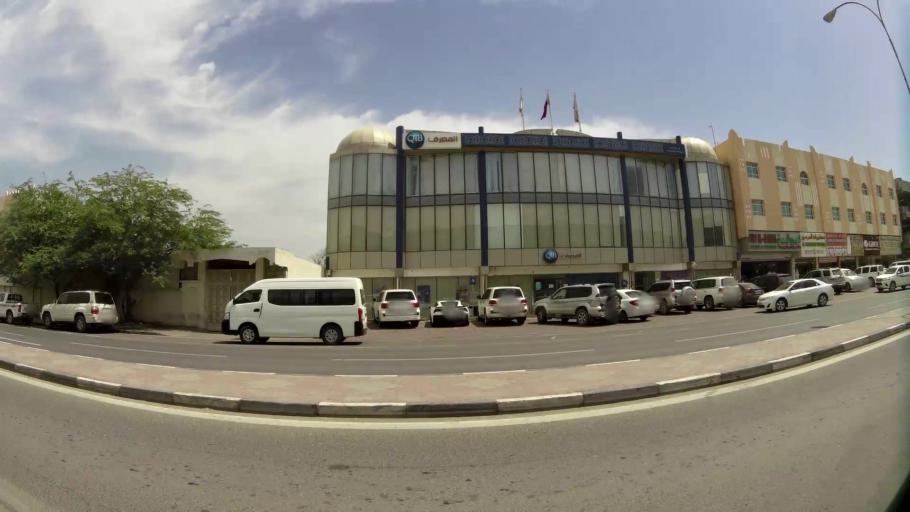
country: QA
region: Baladiyat ar Rayyan
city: Ar Rayyan
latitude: 25.2881
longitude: 51.4203
